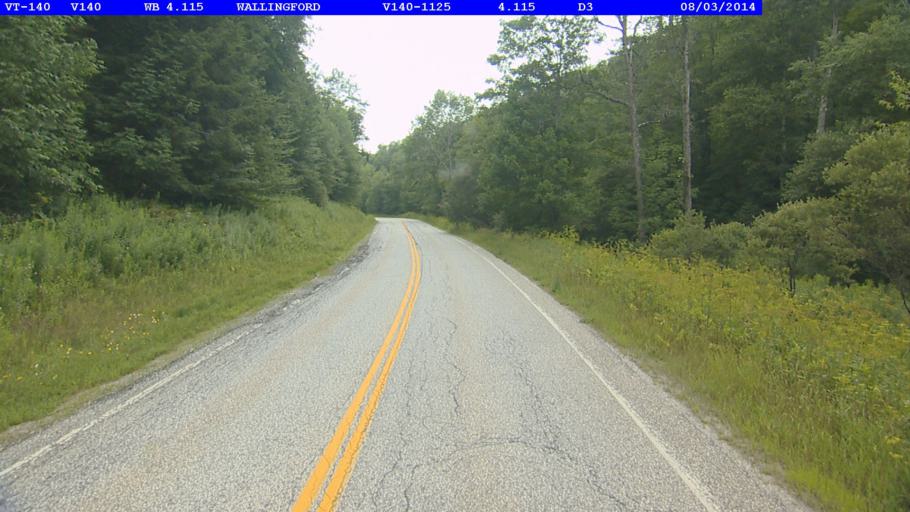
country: US
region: Vermont
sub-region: Rutland County
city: Rutland
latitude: 43.4601
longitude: -72.9087
